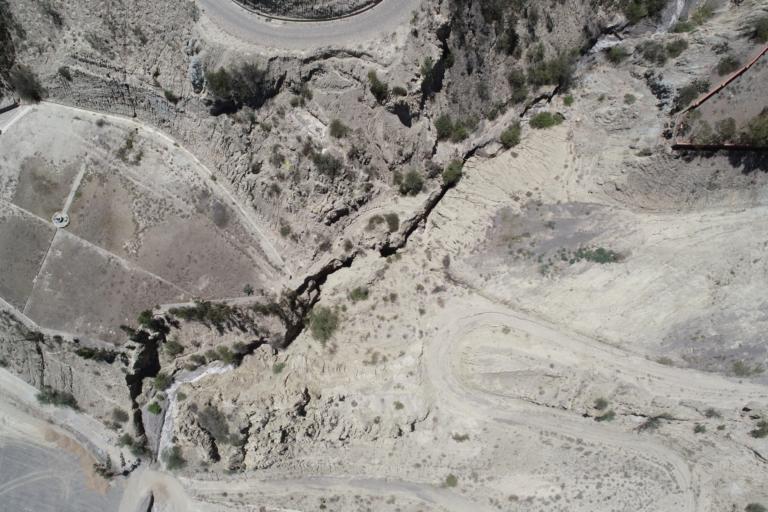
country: BO
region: La Paz
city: La Paz
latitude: -16.6193
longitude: -68.0594
